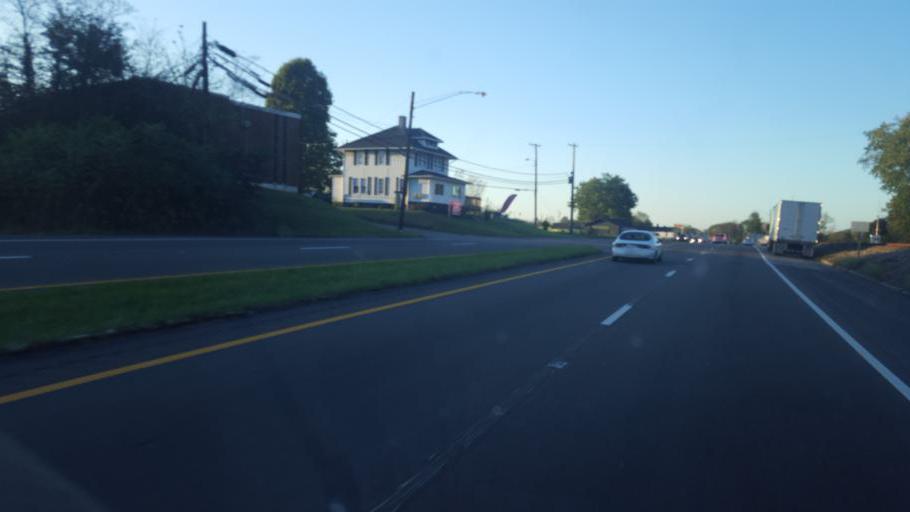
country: US
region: Ohio
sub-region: Scioto County
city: Lucasville
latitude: 38.8728
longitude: -82.9952
